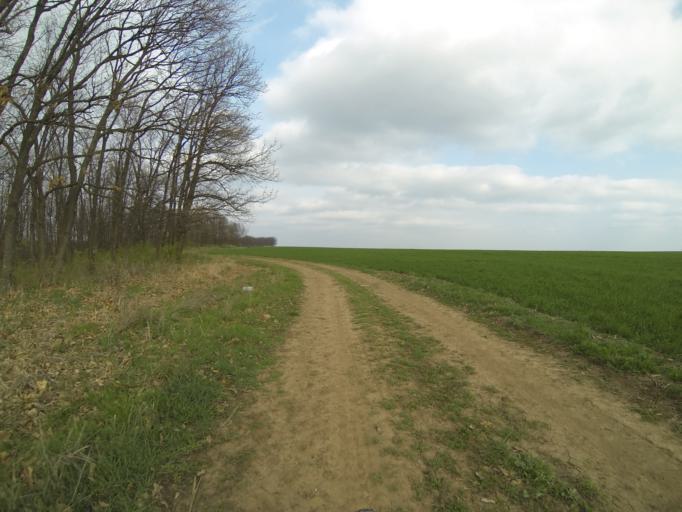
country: RO
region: Dolj
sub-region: Comuna Podari
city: Podari
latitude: 44.2415
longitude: 23.7194
